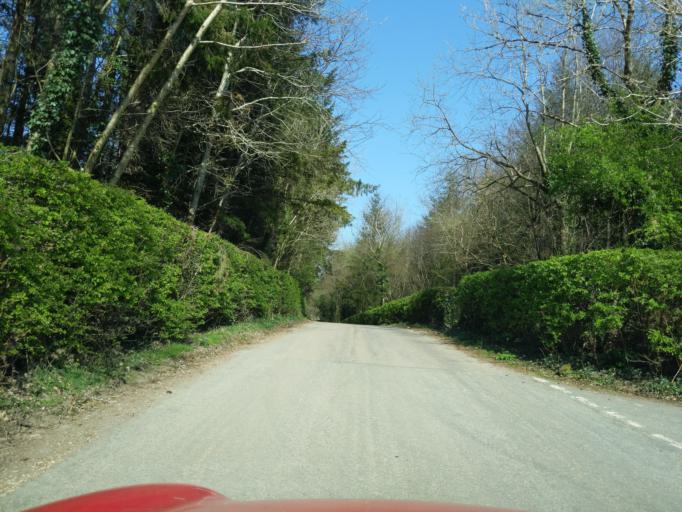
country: GB
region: England
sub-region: Devon
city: Bere Alston
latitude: 50.4616
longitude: -4.1397
